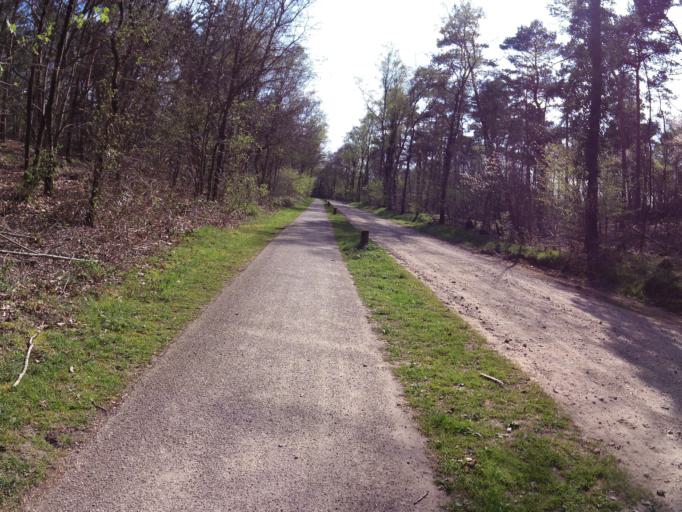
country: NL
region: Gelderland
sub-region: Gemeente Nijmegen
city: Lindenholt
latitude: 51.7738
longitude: 5.8242
